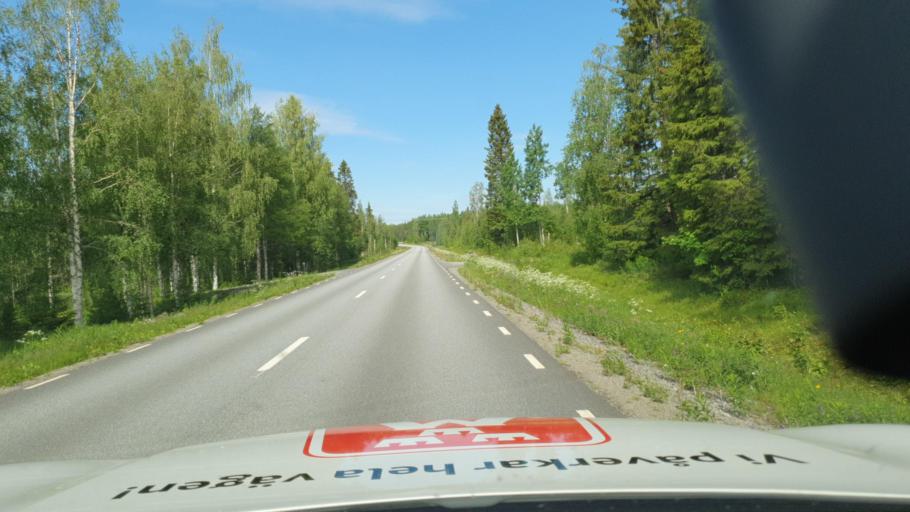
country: SE
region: Vaesterbotten
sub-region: Skelleftea Kommun
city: Forsbacka
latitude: 64.7200
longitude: 20.4175
